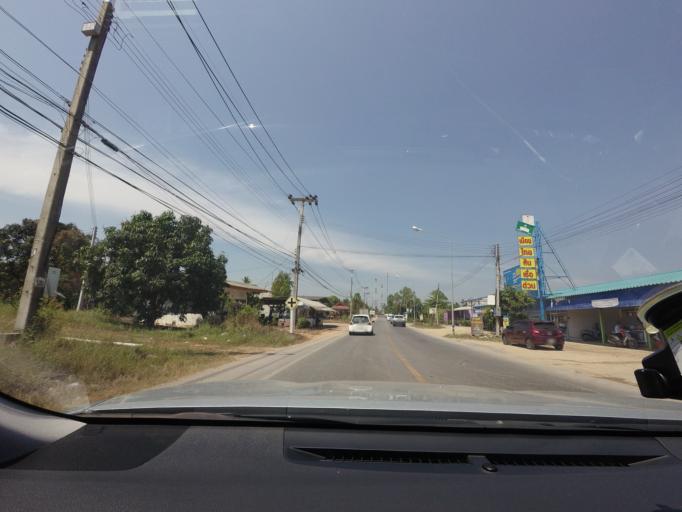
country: TH
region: Surat Thani
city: Phunphin
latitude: 9.1916
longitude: 99.2552
